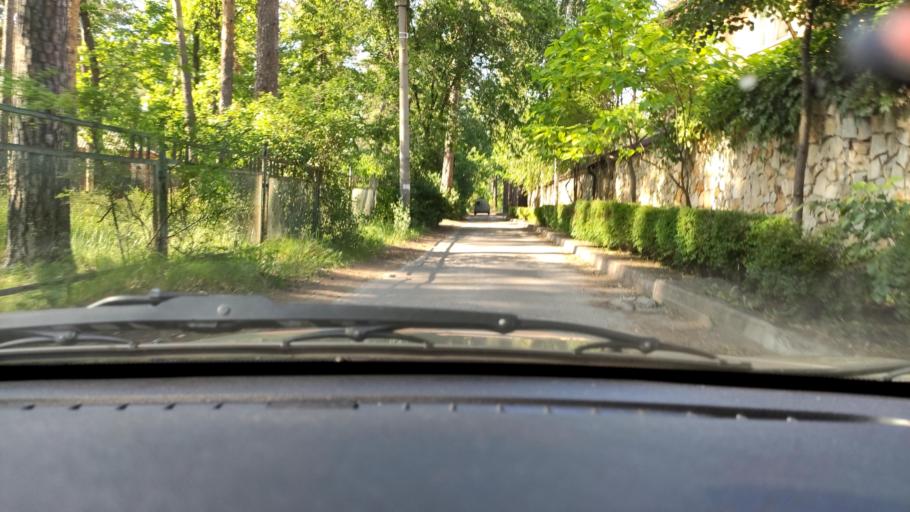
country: RU
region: Voronezj
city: Somovo
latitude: 51.7498
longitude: 39.3743
